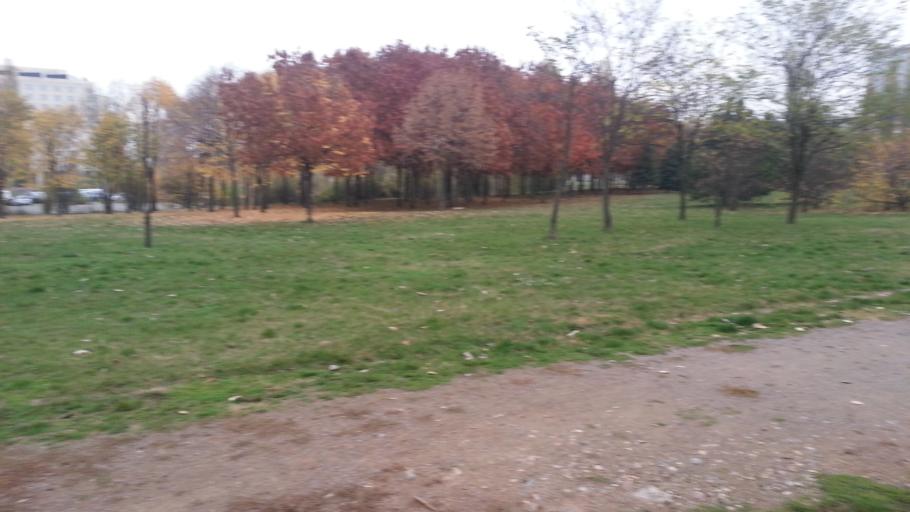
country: BG
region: Sofia-Capital
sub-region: Stolichna Obshtina
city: Sofia
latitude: 42.6798
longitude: 23.3168
